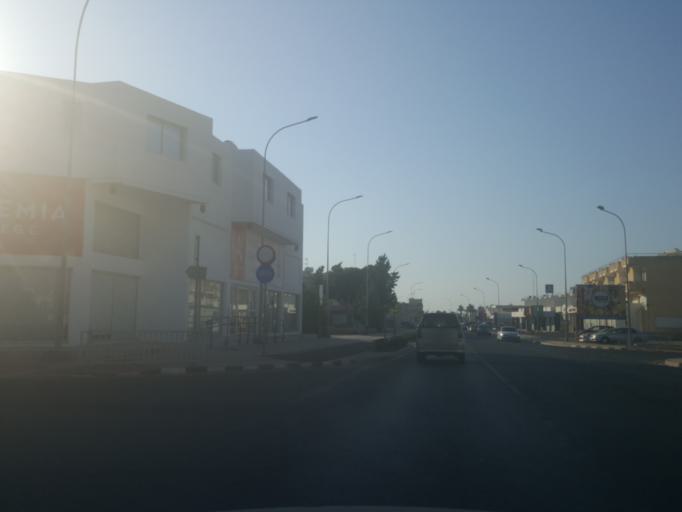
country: CY
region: Ammochostos
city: Deryneia
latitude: 35.0549
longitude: 33.9720
